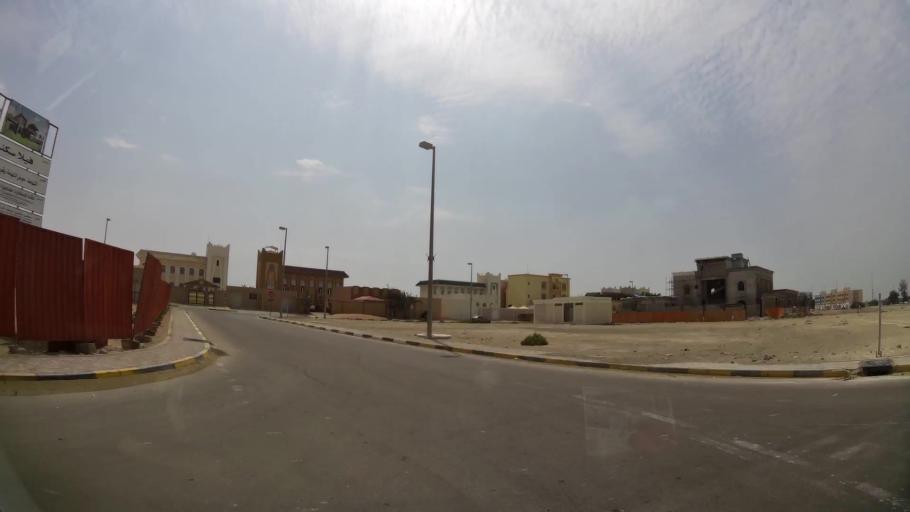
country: AE
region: Abu Dhabi
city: Abu Dhabi
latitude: 24.5333
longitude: 54.6841
